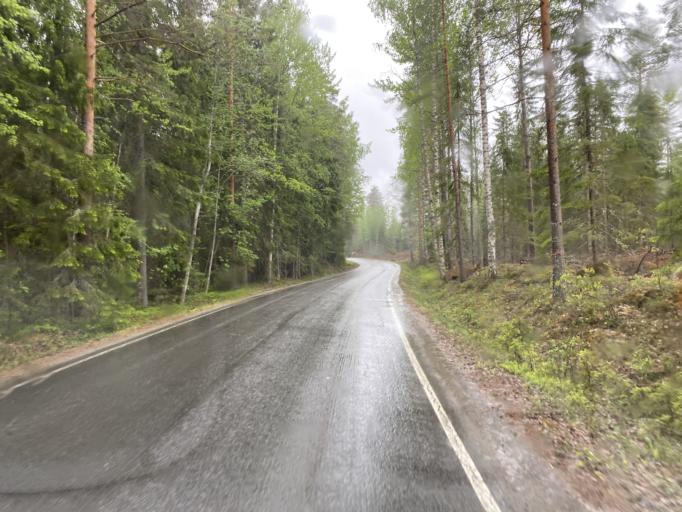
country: FI
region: Haeme
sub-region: Forssa
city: Humppila
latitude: 61.0878
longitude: 23.3092
